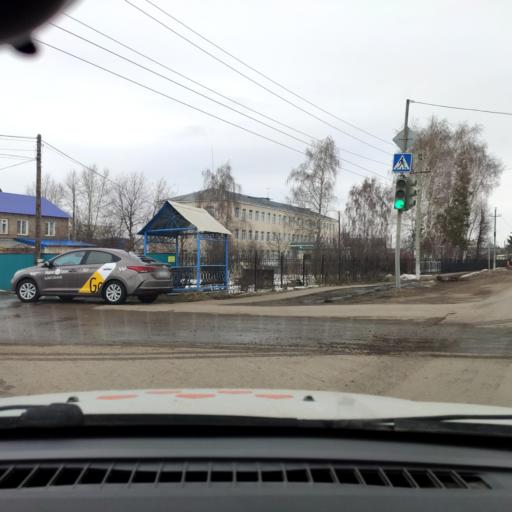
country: RU
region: Bashkortostan
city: Kushnarenkovo
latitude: 55.1041
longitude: 55.3438
